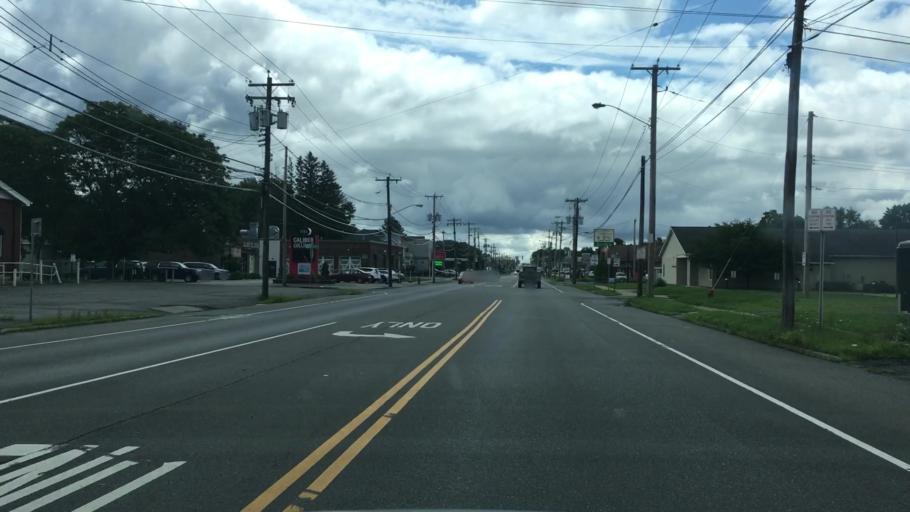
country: US
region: New York
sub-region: Schenectady County
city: Schenectady
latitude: 42.7829
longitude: -73.9069
